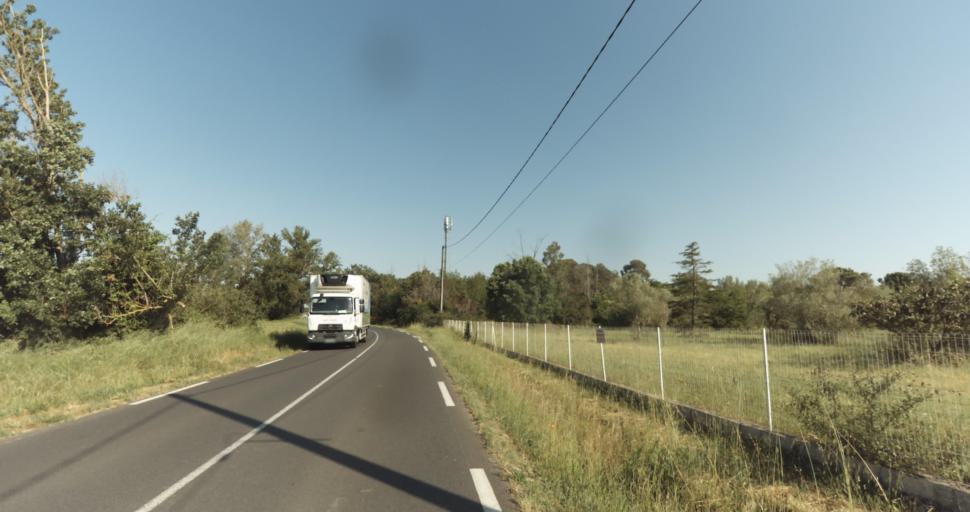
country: FR
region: Midi-Pyrenees
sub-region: Departement de la Haute-Garonne
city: Plaisance-du-Touch
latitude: 43.5509
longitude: 1.3155
